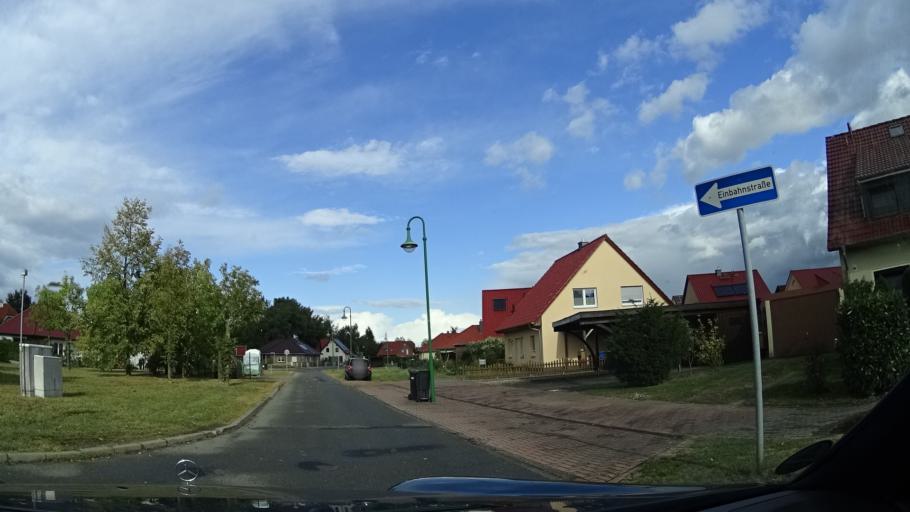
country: DE
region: Brandenburg
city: Neuruppin
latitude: 52.8925
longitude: 12.7924
